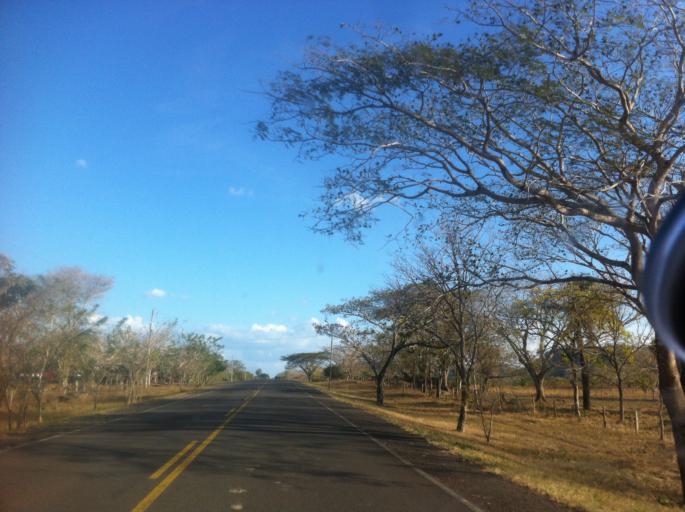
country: NI
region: Rio San Juan
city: Morrito
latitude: 11.7818
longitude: -85.0204
